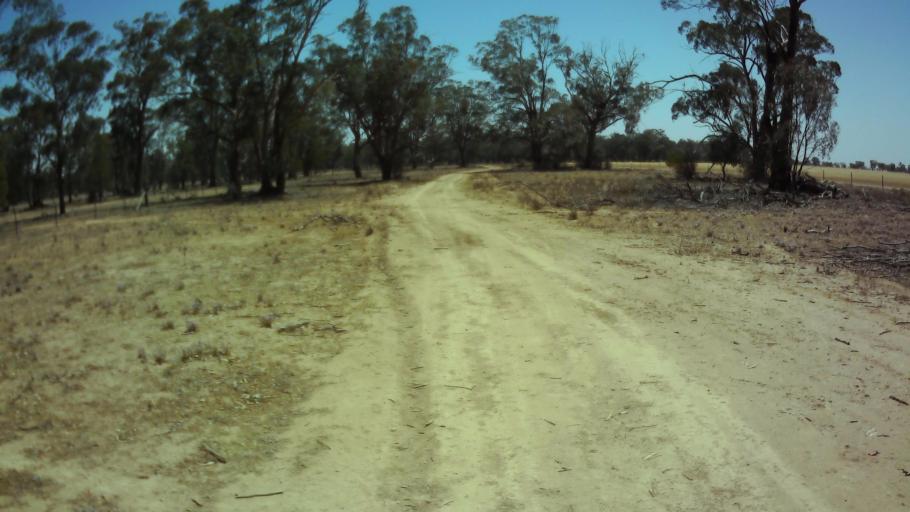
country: AU
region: New South Wales
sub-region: Weddin
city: Grenfell
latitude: -34.0684
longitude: 147.7955
